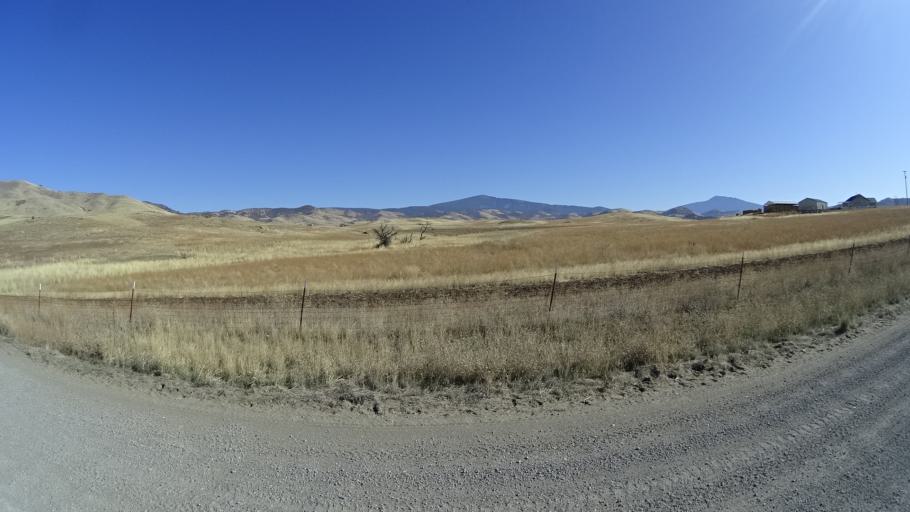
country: US
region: California
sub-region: Siskiyou County
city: Montague
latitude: 41.8265
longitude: -122.4206
